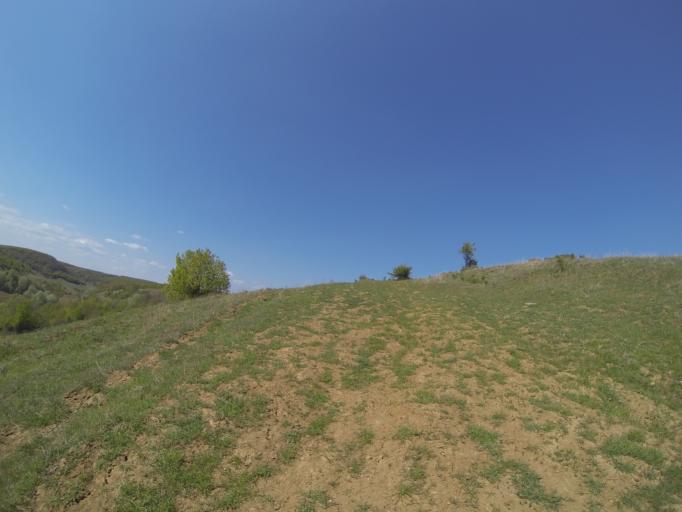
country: RO
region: Gorj
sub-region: Comuna Crusetu
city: Crusetu
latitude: 44.6069
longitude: 23.6506
